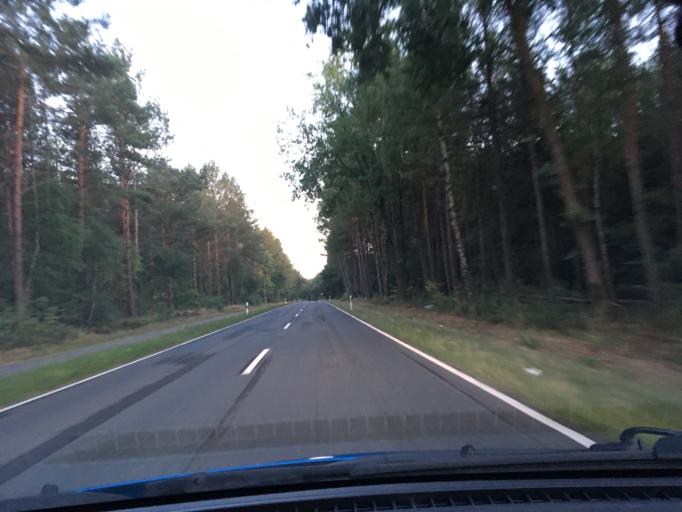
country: DE
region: Lower Saxony
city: Fassberg
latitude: 52.9076
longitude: 10.1528
